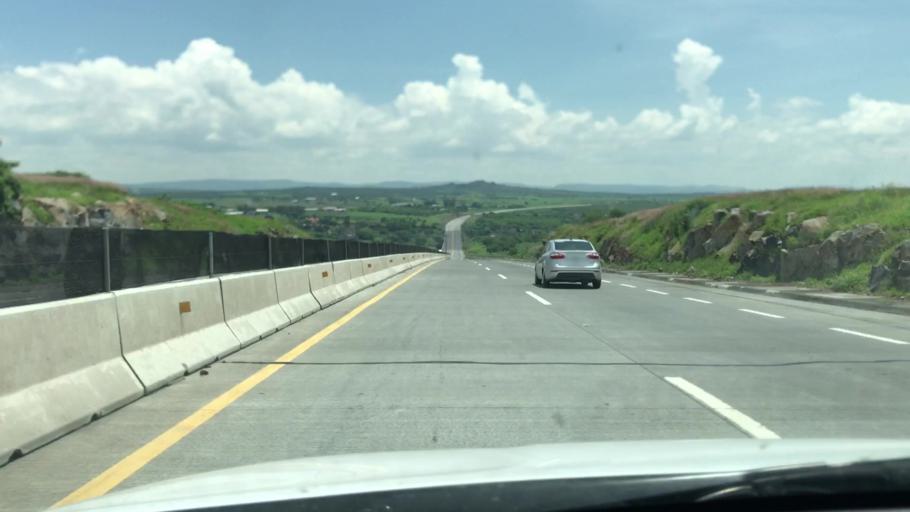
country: MX
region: Jalisco
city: Degollado
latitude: 20.3703
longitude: -102.1268
